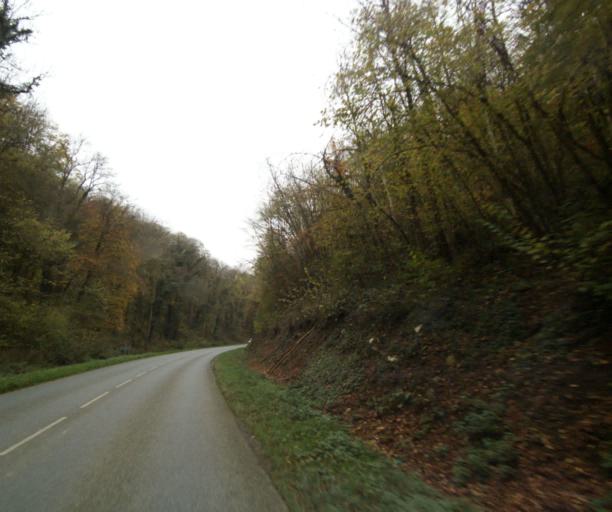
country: FR
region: Lorraine
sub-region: Departement de Meurthe-et-Moselle
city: Joeuf
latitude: 49.2476
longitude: 6.0176
